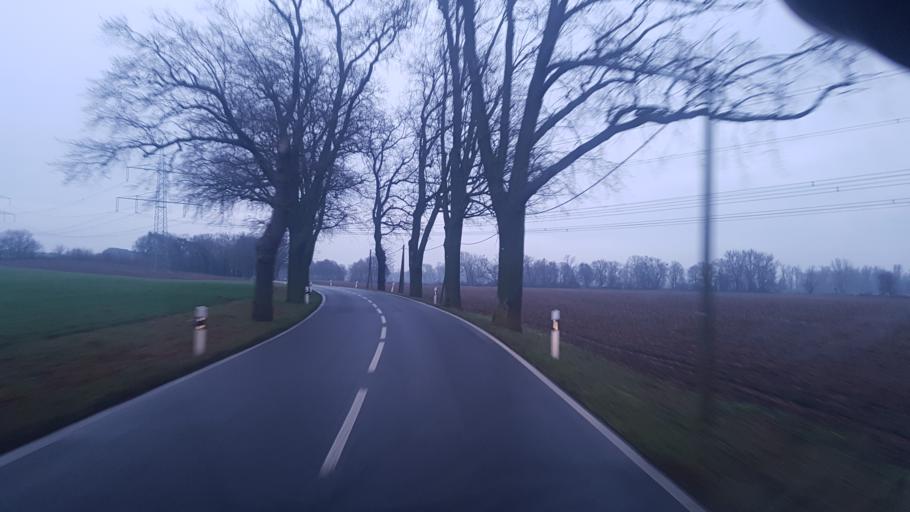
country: DE
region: Brandenburg
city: Trebbin
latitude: 52.2462
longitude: 13.2127
